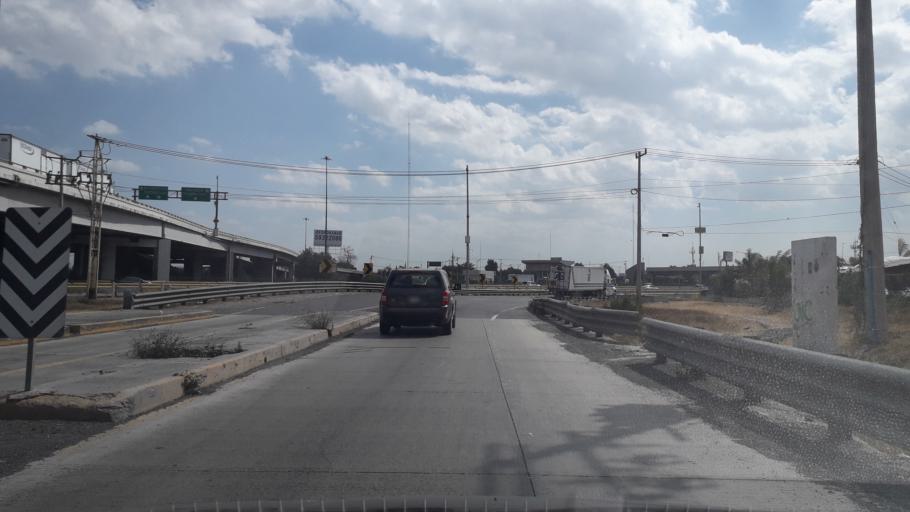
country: MX
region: Mexico
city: Ecatepec
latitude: 19.6055
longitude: -99.0377
